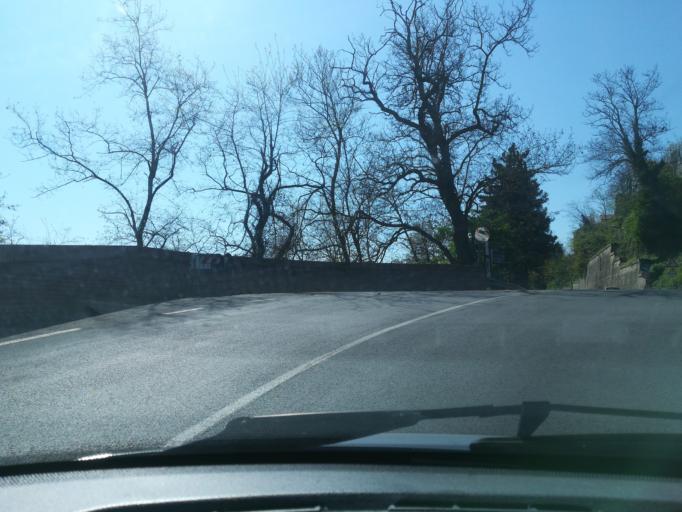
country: IT
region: The Marches
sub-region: Provincia di Macerata
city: Cingoli
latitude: 43.3741
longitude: 13.2194
